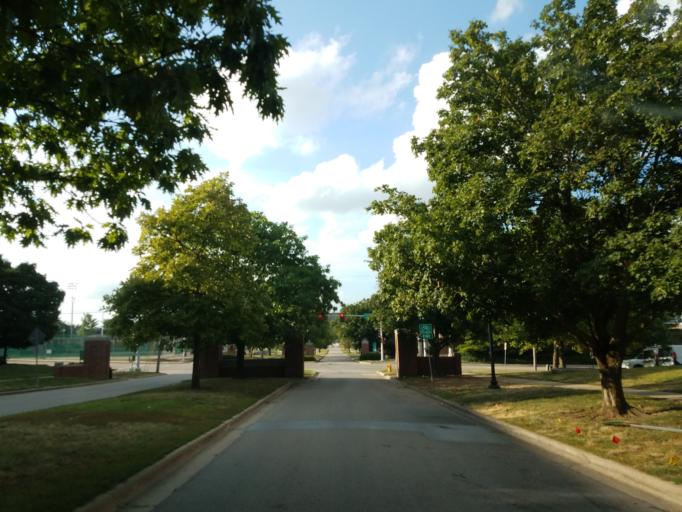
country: US
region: Illinois
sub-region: McLean County
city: Bloomington
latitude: 40.4926
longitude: -88.9908
